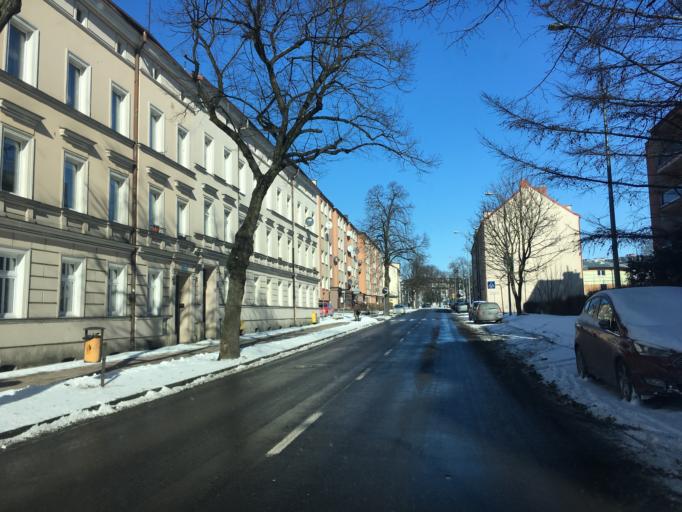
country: PL
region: Pomeranian Voivodeship
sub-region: Slupsk
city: Slupsk
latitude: 54.4610
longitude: 17.0410
